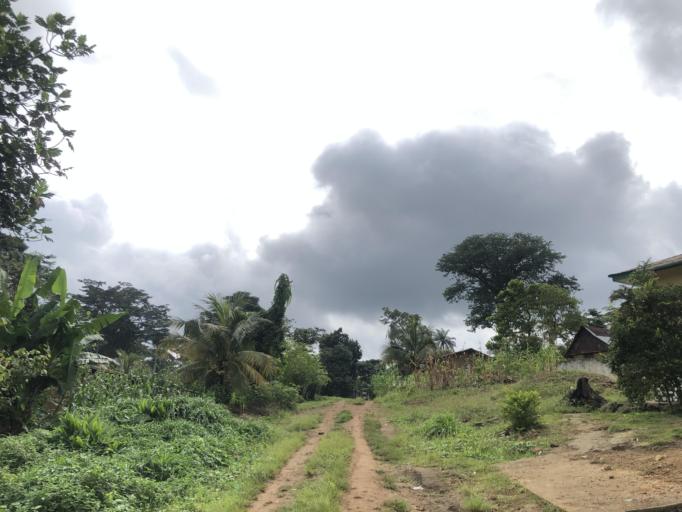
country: SL
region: Eastern Province
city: Kailahun
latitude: 8.2755
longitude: -10.5551
